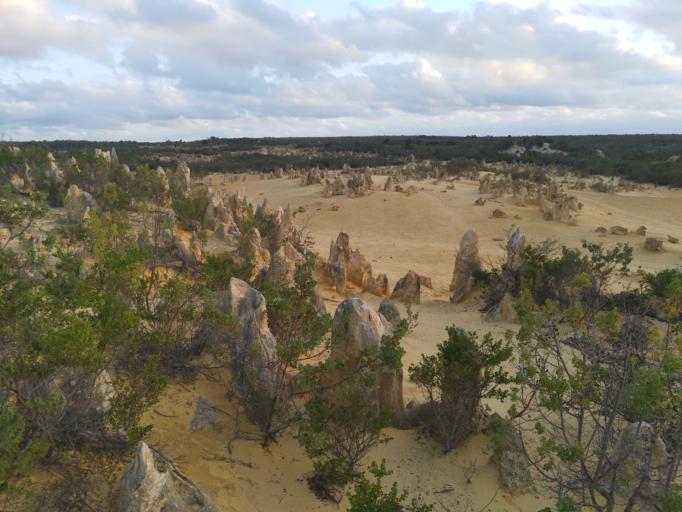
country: AU
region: Western Australia
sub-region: Dandaragan
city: Jurien Bay
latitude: -30.6090
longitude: 115.1631
